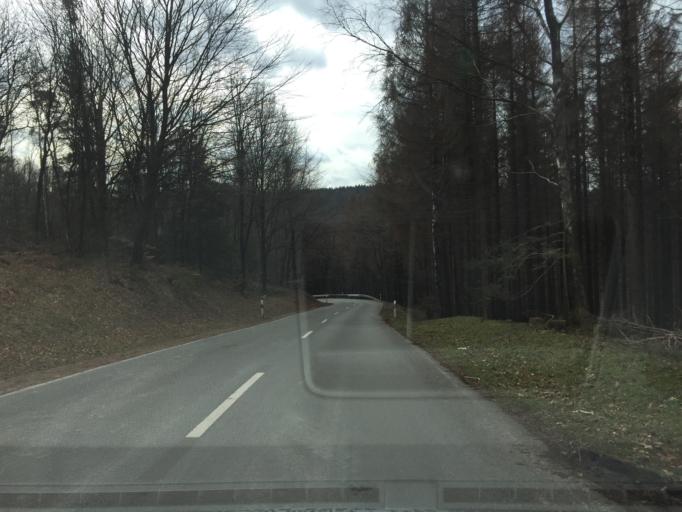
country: DE
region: North Rhine-Westphalia
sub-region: Regierungsbezirk Detmold
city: Detmold
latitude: 51.9066
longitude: 8.8416
